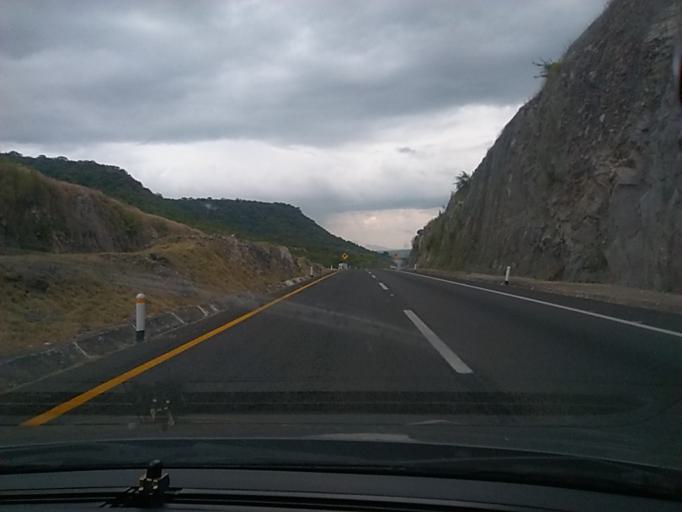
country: MX
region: Jalisco
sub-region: Zapotlan del Rey
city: Zapotlan del Rey
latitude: 20.4754
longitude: -102.9300
